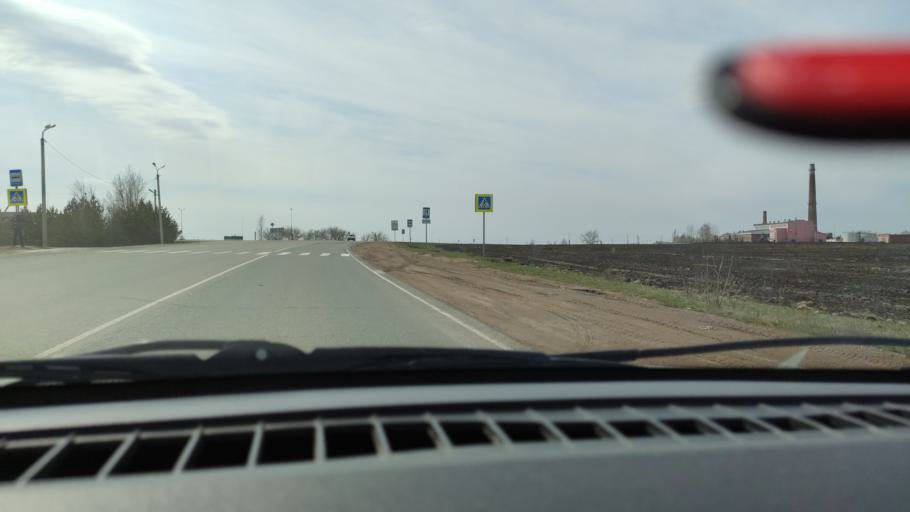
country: RU
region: Bashkortostan
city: Dyurtyuli
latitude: 55.5003
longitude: 54.8297
